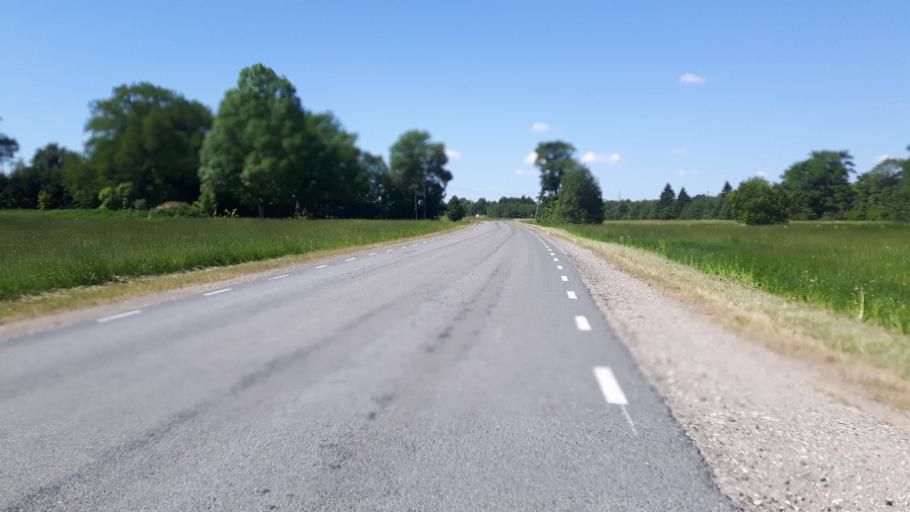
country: EE
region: Paernumaa
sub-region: Tootsi vald
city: Tootsi
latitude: 58.4958
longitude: 24.8845
